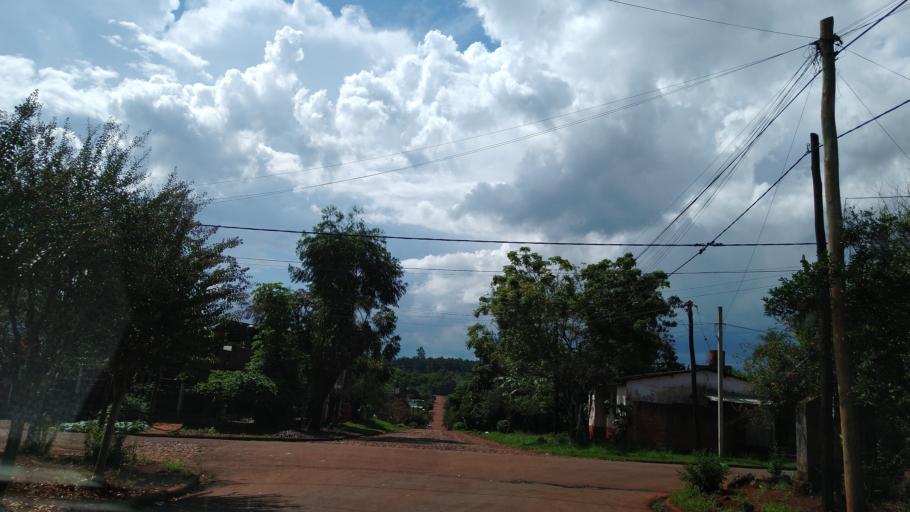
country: AR
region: Misiones
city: Puerto Libertad
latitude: -25.9689
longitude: -54.5771
